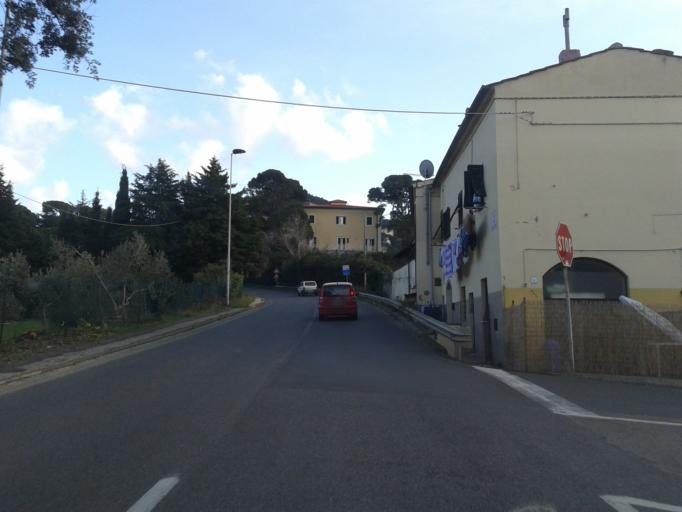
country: IT
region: Tuscany
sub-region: Provincia di Livorno
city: Quercianella
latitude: 43.4997
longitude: 10.3427
